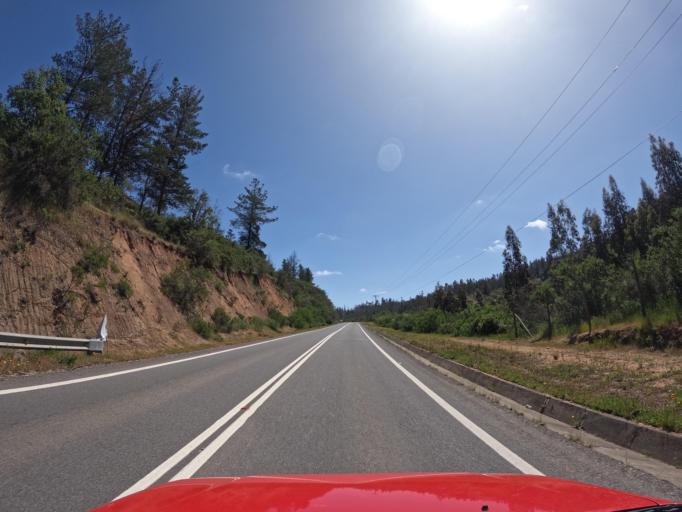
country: CL
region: O'Higgins
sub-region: Provincia de Colchagua
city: Santa Cruz
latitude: -34.6869
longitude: -71.7859
